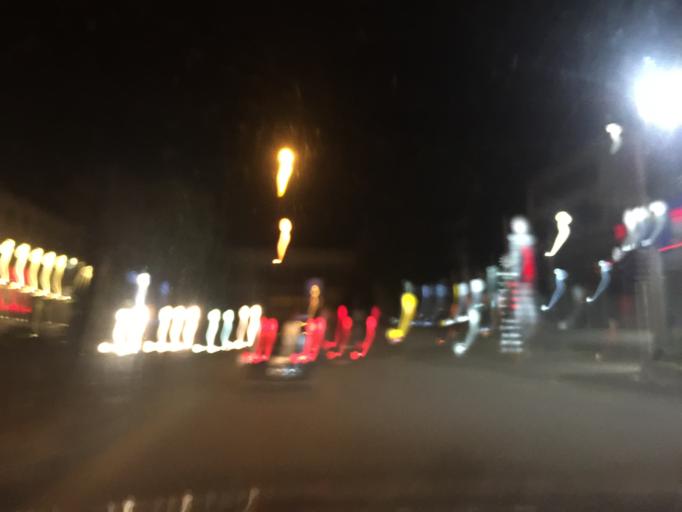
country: JO
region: Amman
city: Al Jubayhah
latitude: 32.0279
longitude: 35.8594
